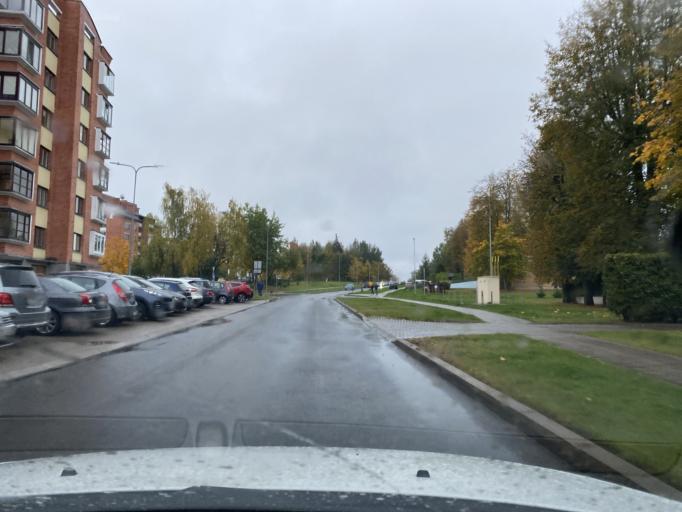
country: LT
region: Vilnius County
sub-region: Vilnius
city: Fabijoniskes
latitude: 54.7447
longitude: 25.2696
